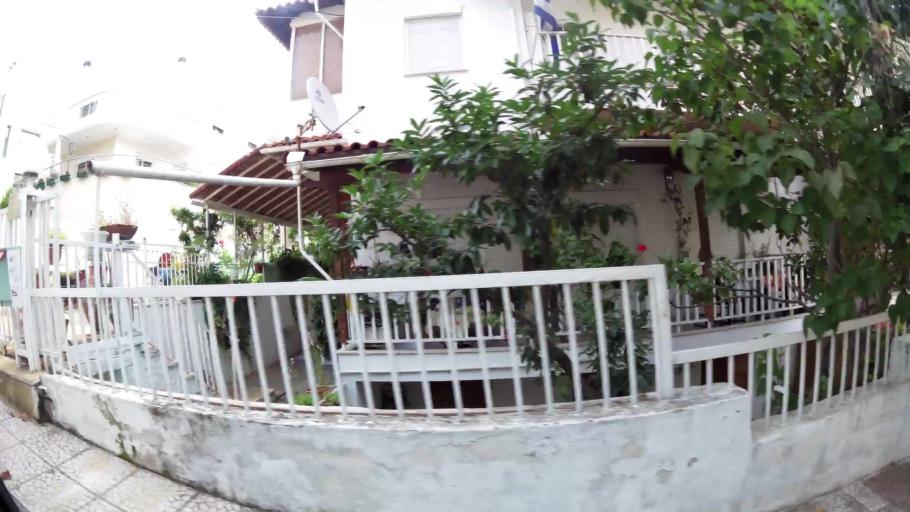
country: GR
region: Central Macedonia
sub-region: Nomos Thessalonikis
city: Panorama
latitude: 40.5886
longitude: 23.0394
